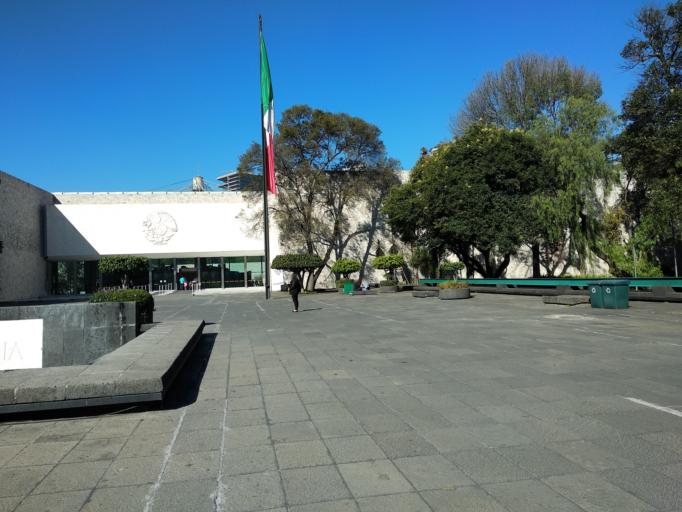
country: MX
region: Mexico City
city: Polanco
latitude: 19.4259
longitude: -99.1848
